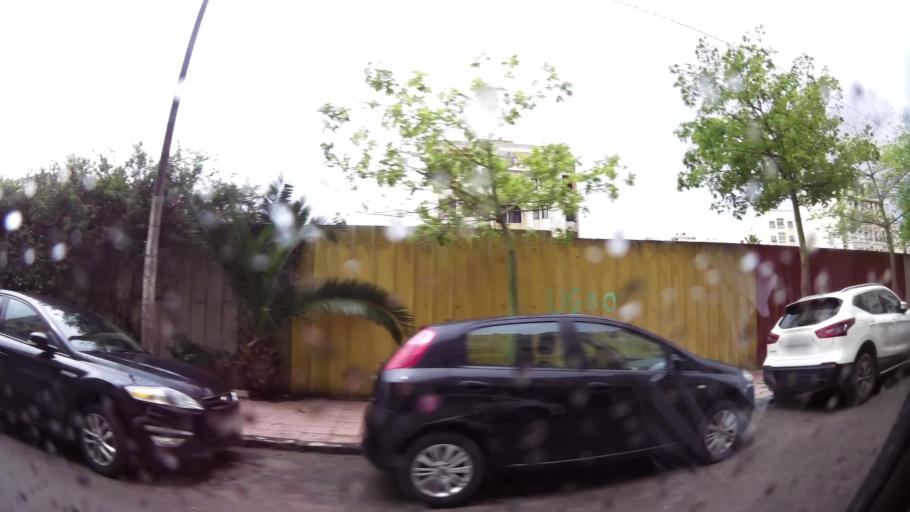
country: MA
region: Grand Casablanca
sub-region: Casablanca
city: Casablanca
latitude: 33.5816
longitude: -7.5990
